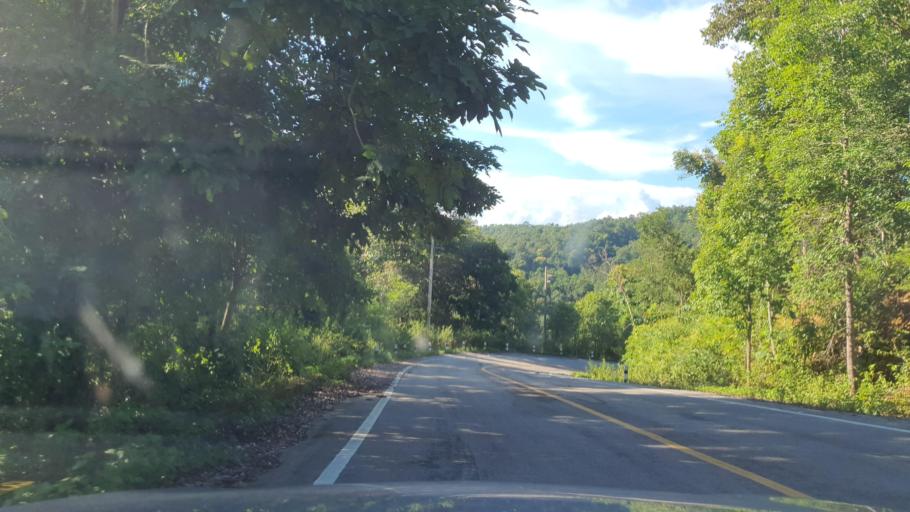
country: TH
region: Chiang Mai
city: Mae On
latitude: 18.7992
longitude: 99.3003
